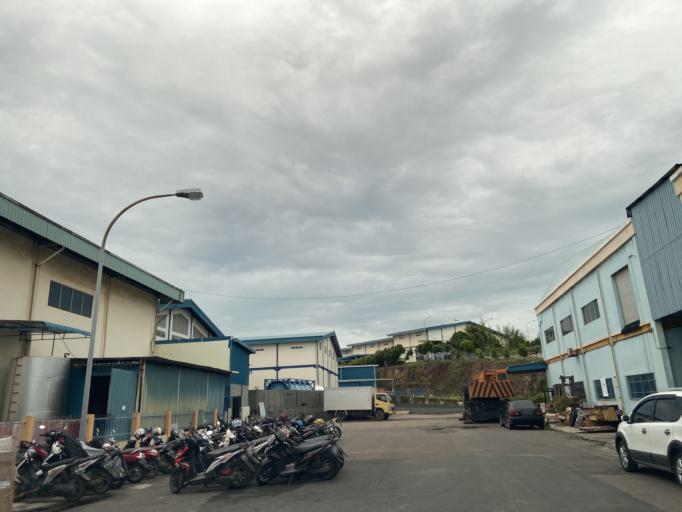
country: SG
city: Singapore
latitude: 1.1657
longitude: 104.0168
